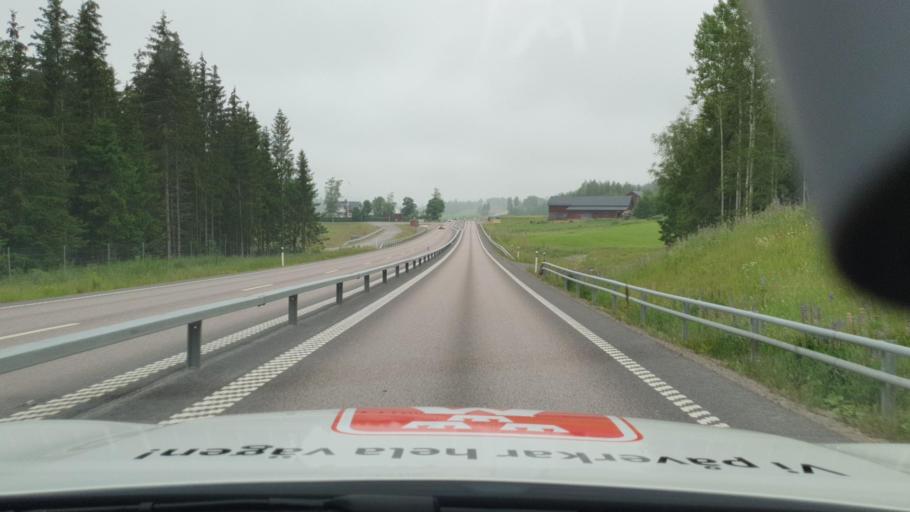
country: SE
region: Vaermland
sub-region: Karlstads Kommun
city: Edsvalla
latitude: 59.5458
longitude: 13.1985
